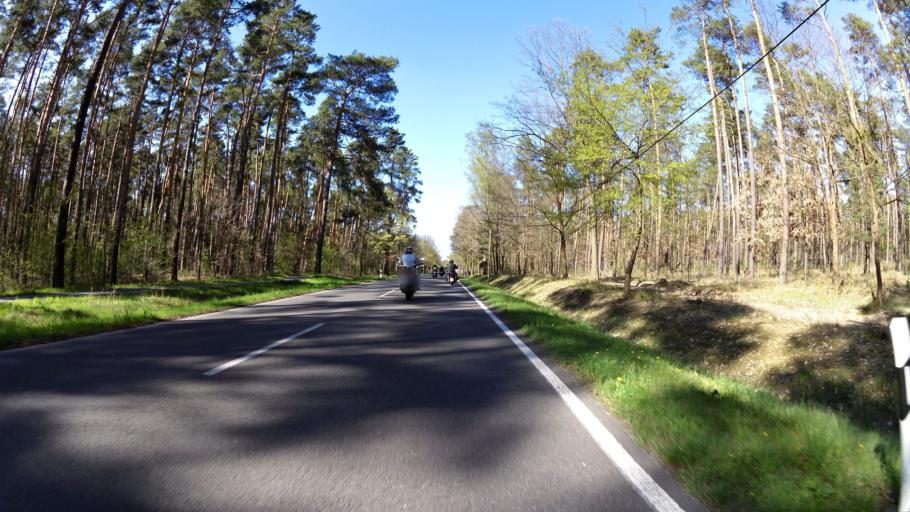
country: DE
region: Brandenburg
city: Grunheide
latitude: 52.4035
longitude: 13.8250
